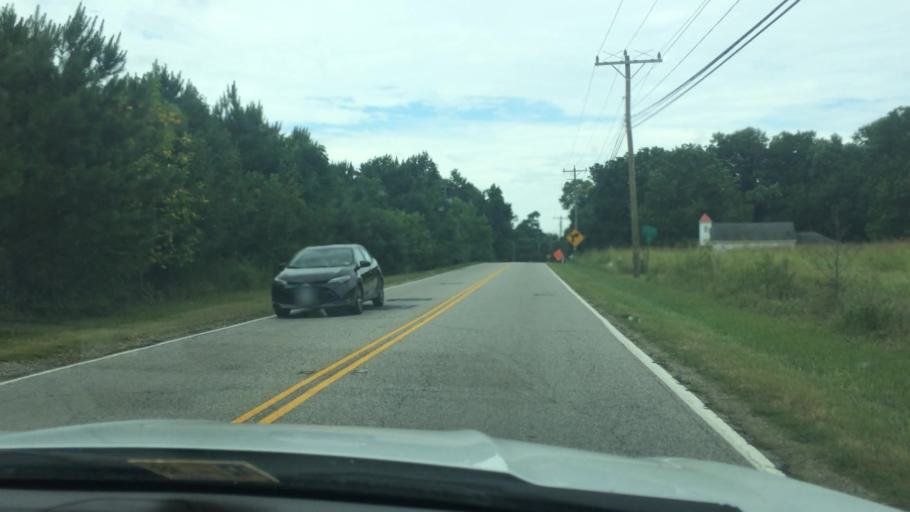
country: US
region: Virginia
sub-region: York County
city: Yorktown
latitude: 37.2074
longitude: -76.6028
